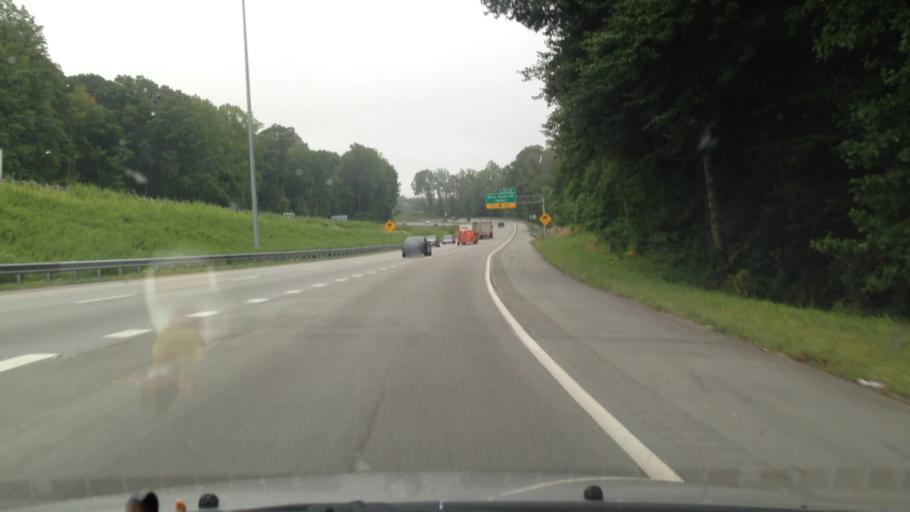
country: US
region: North Carolina
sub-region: Forsyth County
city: Kernersville
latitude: 36.1116
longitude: -80.0597
